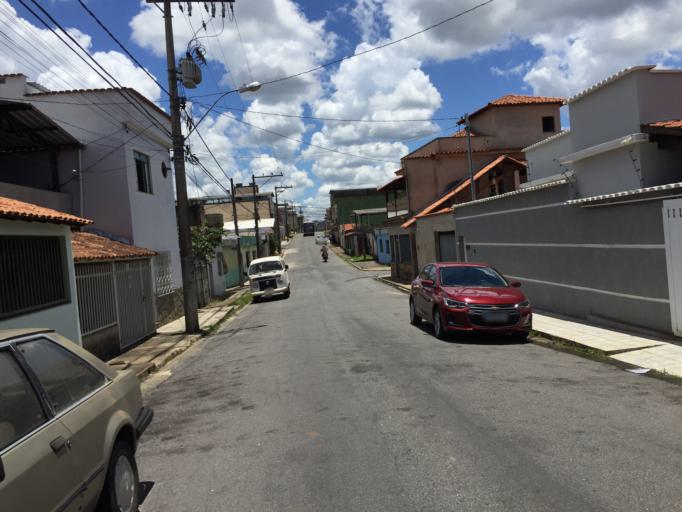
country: BR
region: Minas Gerais
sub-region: Sao Joao Del Rei
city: Sao Joao del Rei
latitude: -21.1441
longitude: -44.2671
